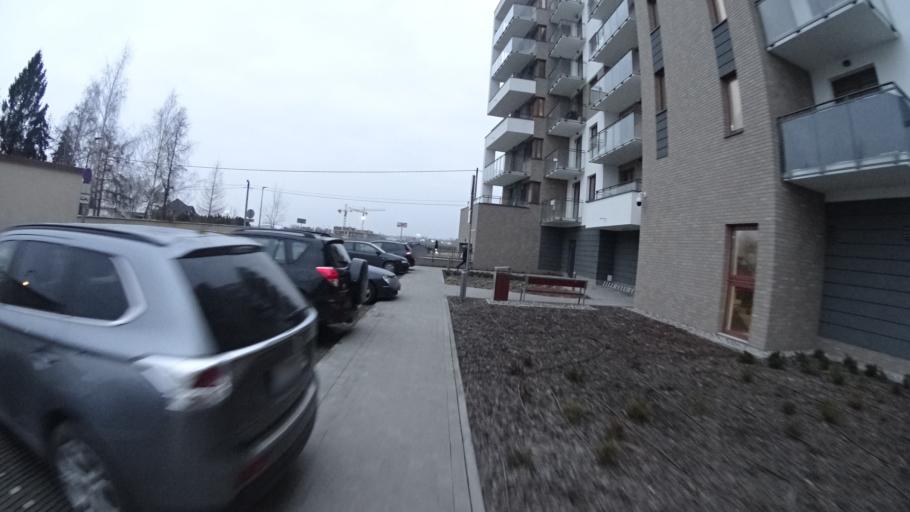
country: PL
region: Masovian Voivodeship
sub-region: Warszawa
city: Ursus
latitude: 52.2269
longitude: 20.8858
